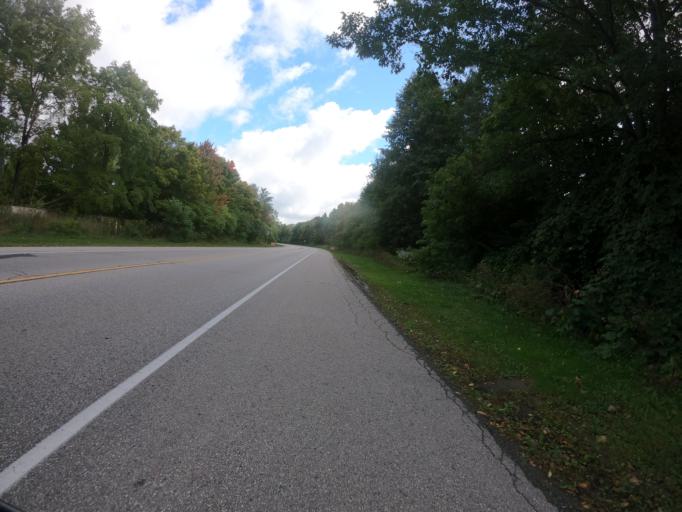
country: CA
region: Ontario
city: Waterloo
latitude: 43.4529
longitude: -80.5416
